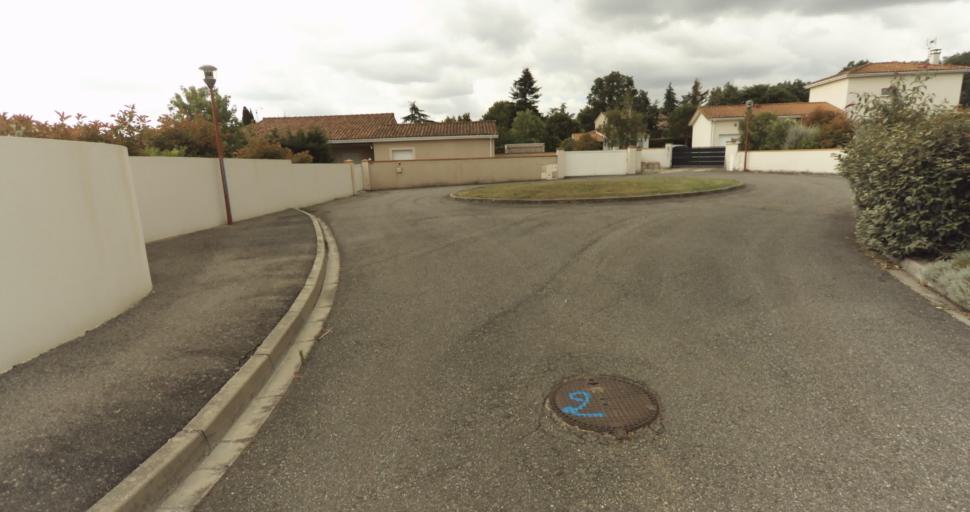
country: FR
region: Midi-Pyrenees
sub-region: Departement de la Haute-Garonne
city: Fonsorbes
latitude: 43.5523
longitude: 1.2282
